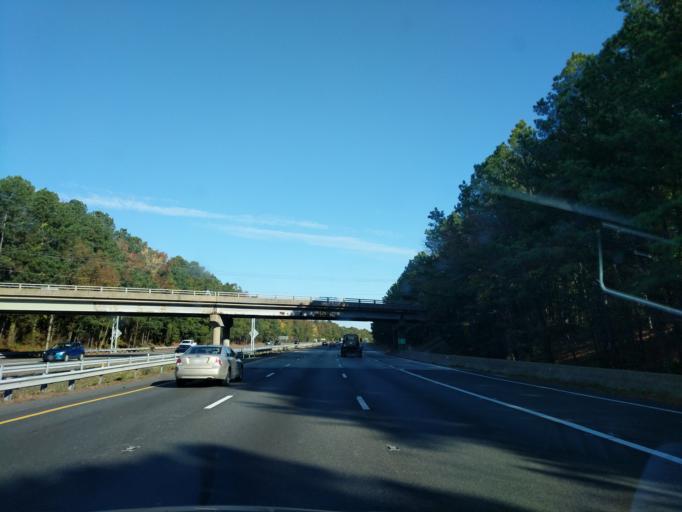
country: US
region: Virginia
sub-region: Henrico County
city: Chamberlayne
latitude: 37.6380
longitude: -77.4521
